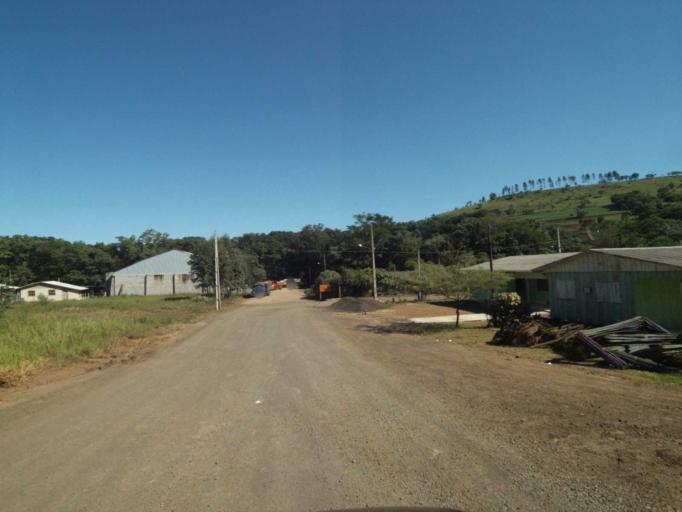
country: BR
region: Parana
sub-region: Francisco Beltrao
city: Francisco Beltrao
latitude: -26.1448
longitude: -53.3142
